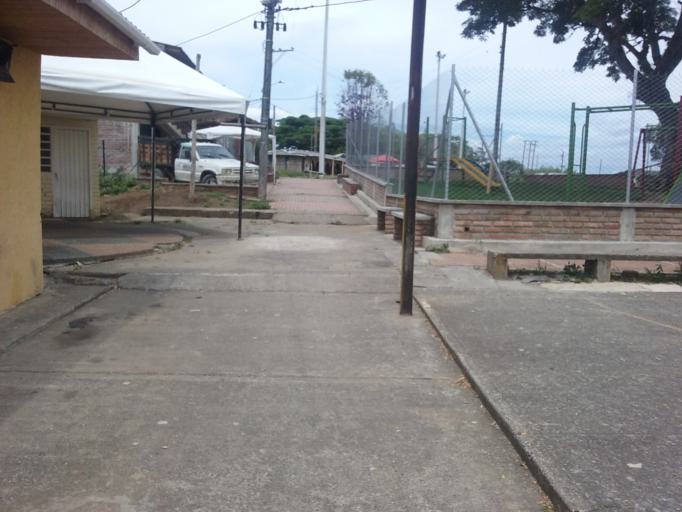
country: CO
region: Valle del Cauca
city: Ulloa
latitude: 4.7247
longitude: -75.7620
